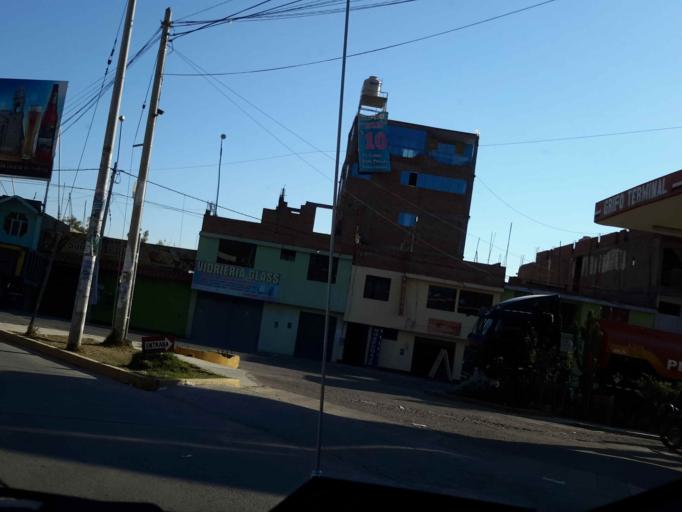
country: PE
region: Ayacucho
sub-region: Provincia de Huamanga
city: Ayacucho
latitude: -13.1349
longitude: -74.2293
